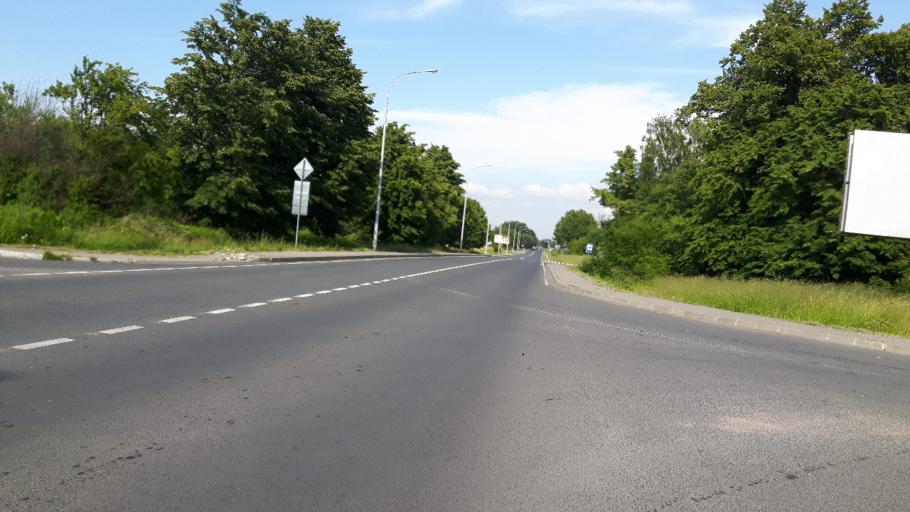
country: RU
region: Kaliningrad
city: Mamonovo
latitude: 54.4647
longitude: 19.9570
